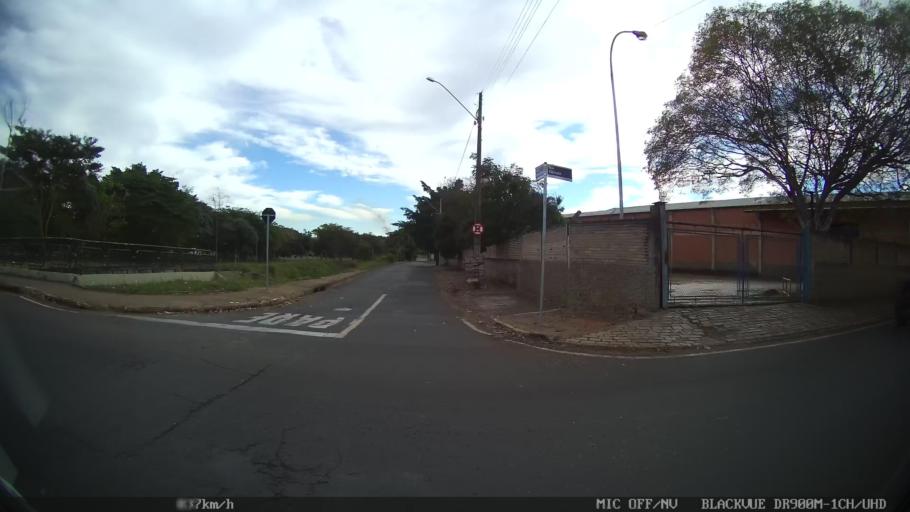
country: BR
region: Sao Paulo
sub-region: Catanduva
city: Catanduva
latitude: -21.1259
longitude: -48.9839
